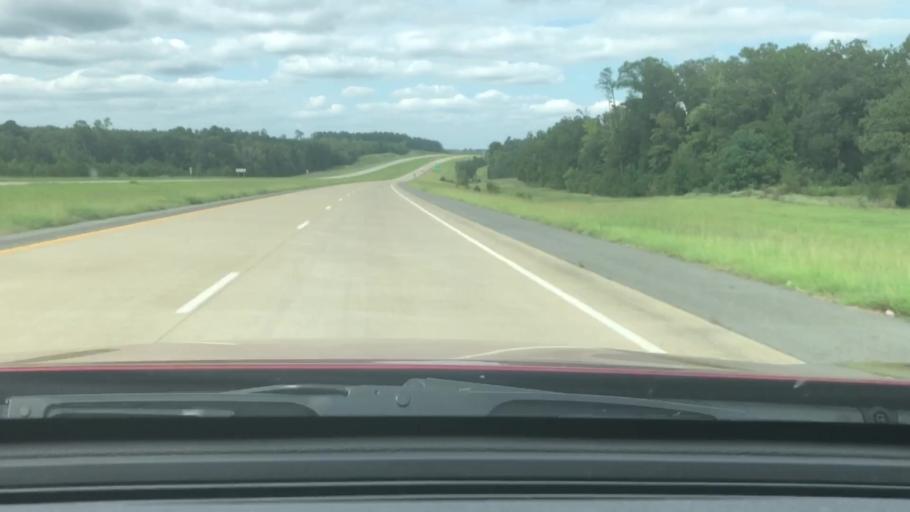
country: US
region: Louisiana
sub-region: Caddo Parish
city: Vivian
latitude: 32.9796
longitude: -93.9093
